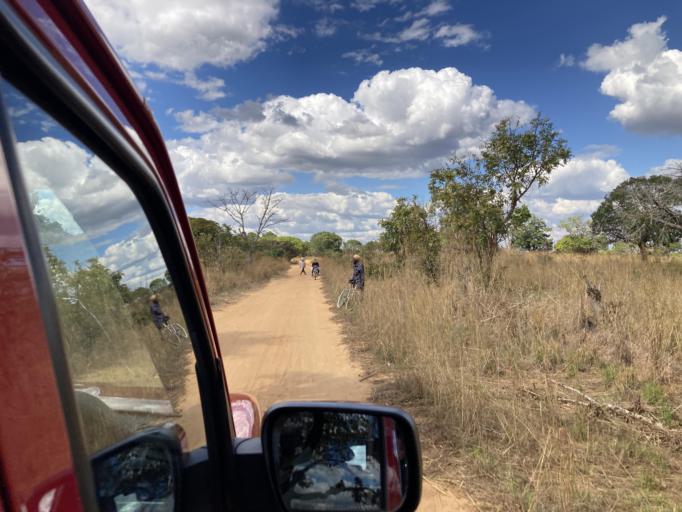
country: MZ
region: Cabo Delgado
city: Montepuez
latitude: -13.1260
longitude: 39.0427
